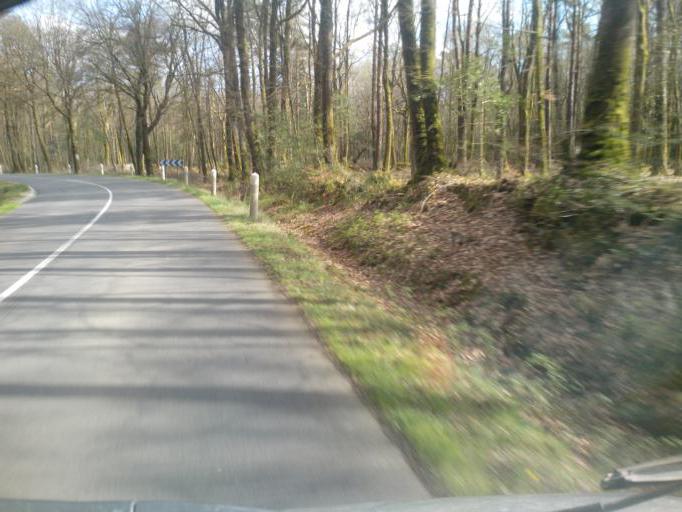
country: FR
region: Brittany
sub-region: Departement d'Ille-et-Vilaine
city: Paimpont
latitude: 48.0145
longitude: -2.1503
